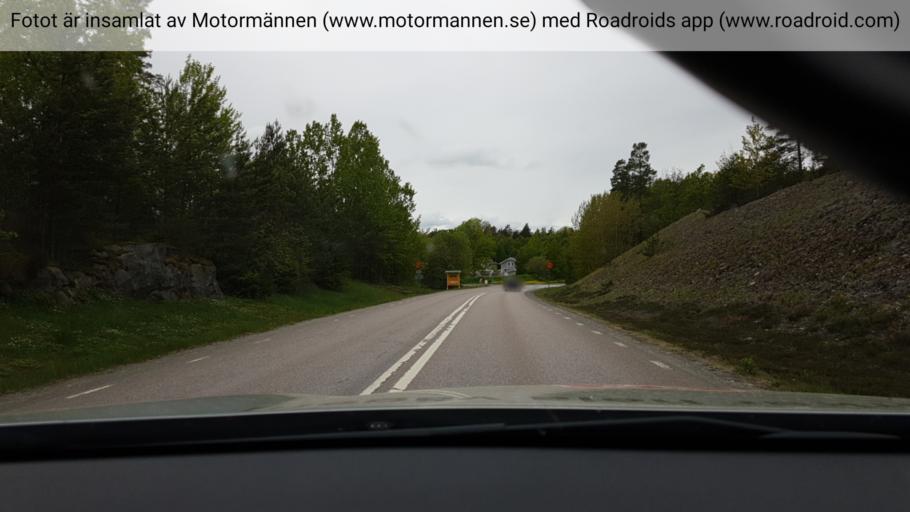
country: SE
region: Stockholm
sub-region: Vaxholms Kommun
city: Vaxholm
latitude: 59.3957
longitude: 18.4013
